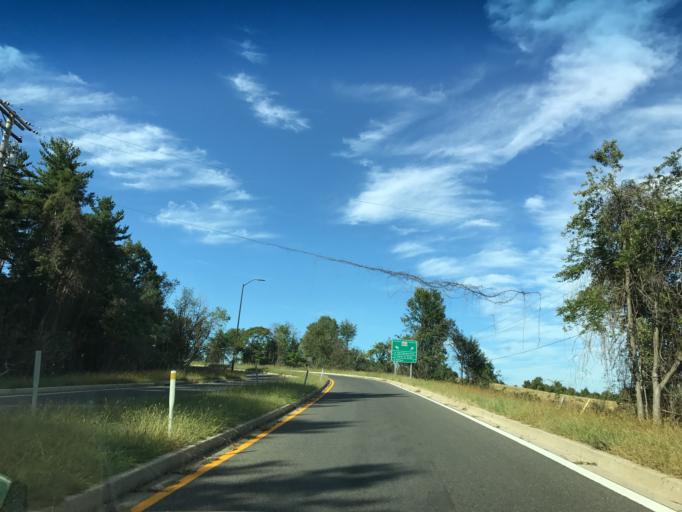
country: US
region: Maryland
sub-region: Anne Arundel County
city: Davidsonville
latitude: 38.9629
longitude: -76.6546
